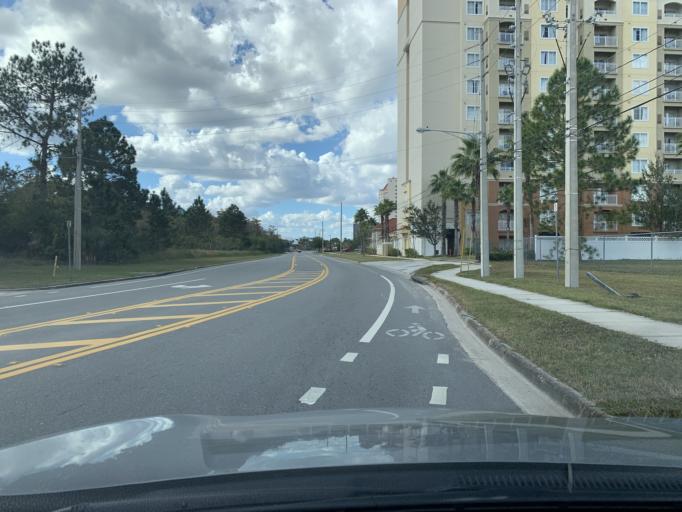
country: US
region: Florida
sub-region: Orange County
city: Tangelo Park
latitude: 28.4563
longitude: -81.4618
